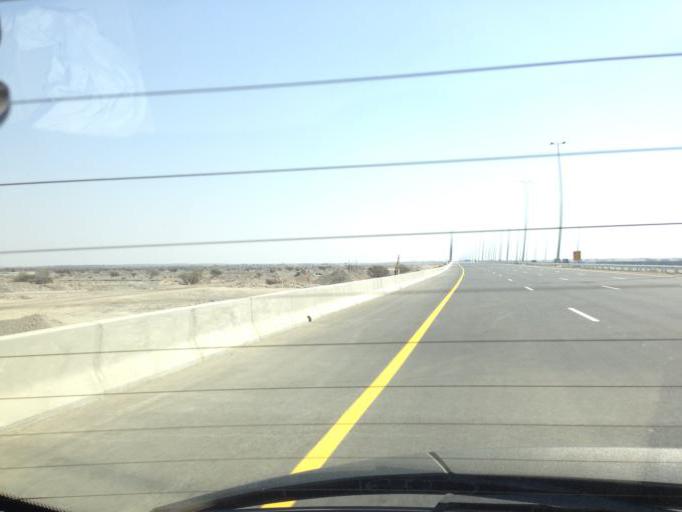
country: OM
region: Al Batinah
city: Rustaq
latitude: 23.5359
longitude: 57.5380
